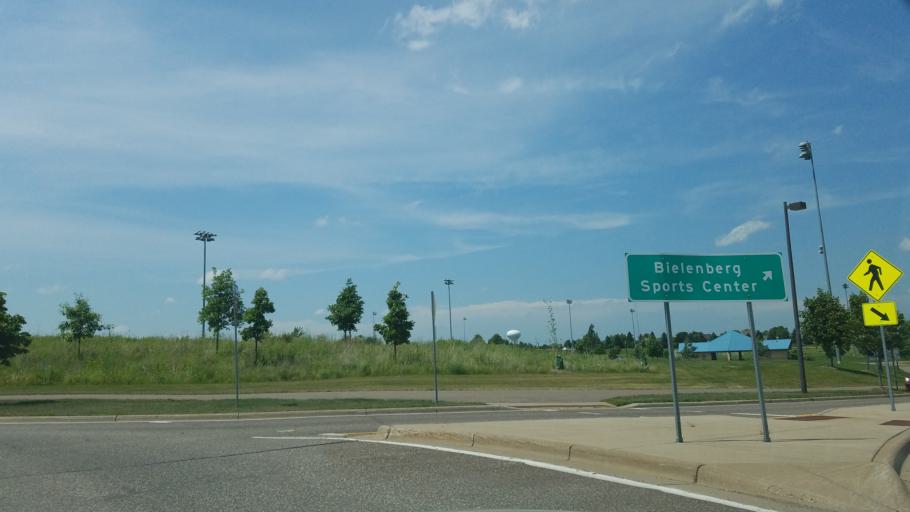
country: US
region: Minnesota
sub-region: Washington County
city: Woodbury
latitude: 44.8873
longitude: -92.9414
